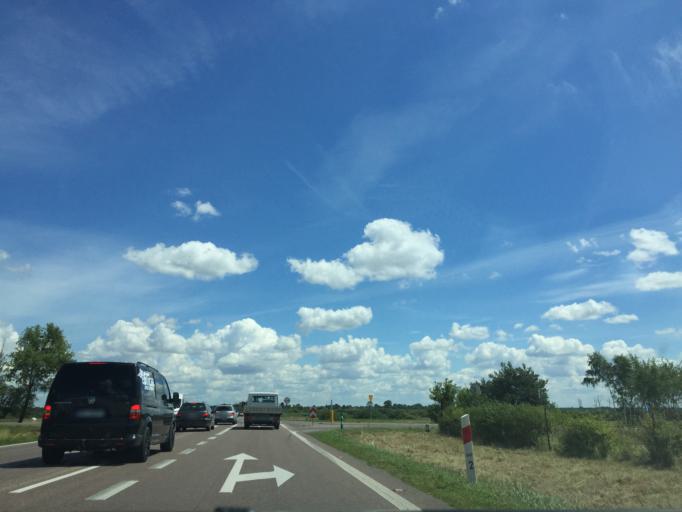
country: PL
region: Lublin Voivodeship
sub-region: Powiat swidnicki
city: Trawniki
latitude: 51.1631
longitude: 23.0290
